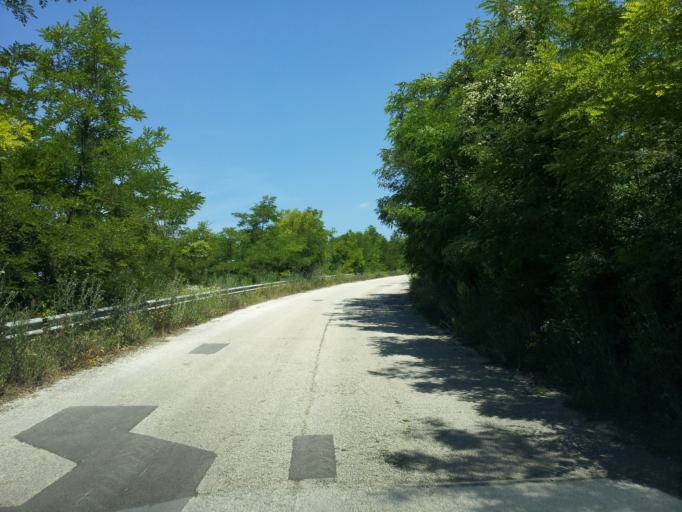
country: HU
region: Fejer
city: Szarliget
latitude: 47.5239
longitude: 18.5486
